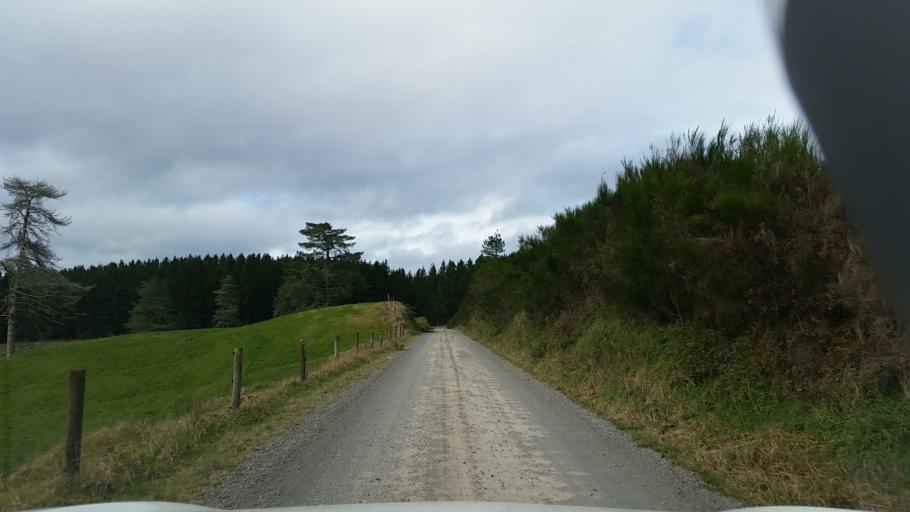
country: NZ
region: Bay of Plenty
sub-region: Whakatane District
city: Murupara
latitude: -38.3429
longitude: 176.5418
